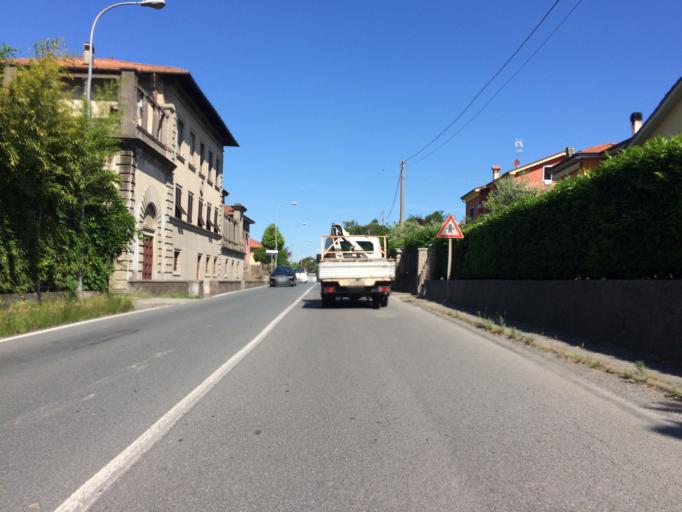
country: IT
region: Tuscany
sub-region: Provincia di Massa-Carrara
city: Borghetto-Melara
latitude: 44.1009
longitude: 9.9814
